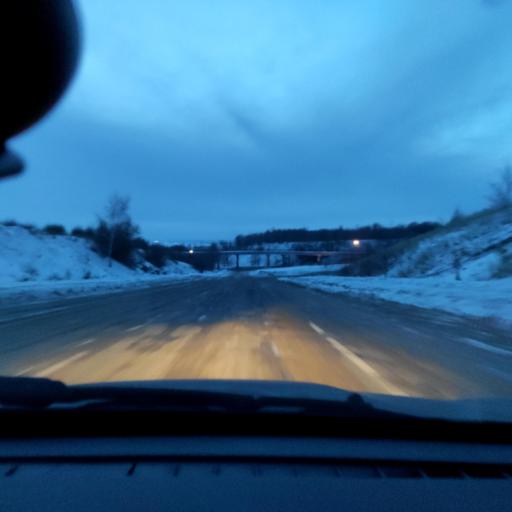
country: RU
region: Samara
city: Tol'yatti
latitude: 53.4969
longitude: 49.2735
